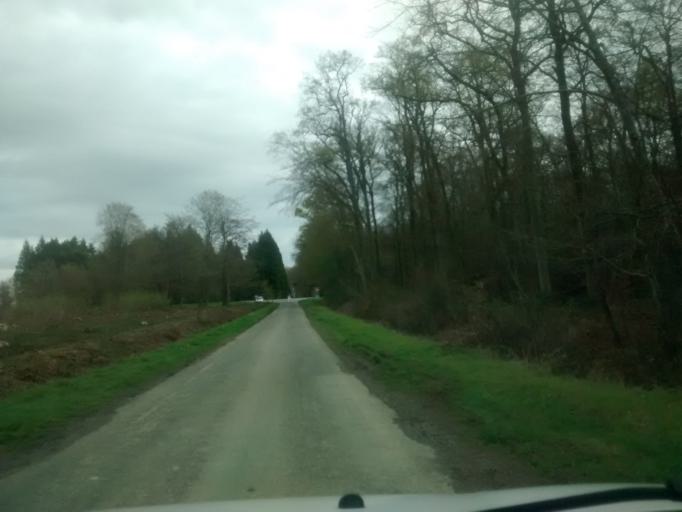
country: FR
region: Brittany
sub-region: Departement d'Ille-et-Vilaine
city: Chasne-sur-Illet
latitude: 48.2331
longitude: -1.5384
